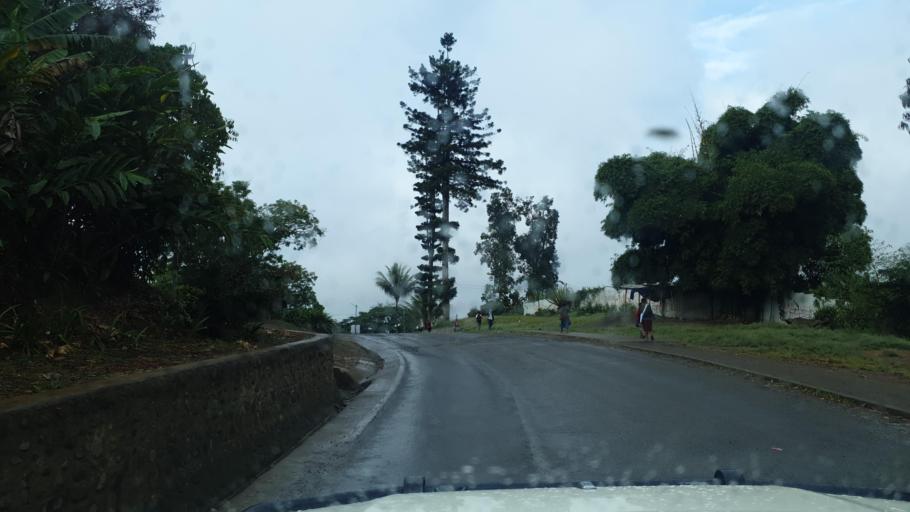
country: PG
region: Eastern Highlands
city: Goroka
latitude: -6.0708
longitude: 145.3919
